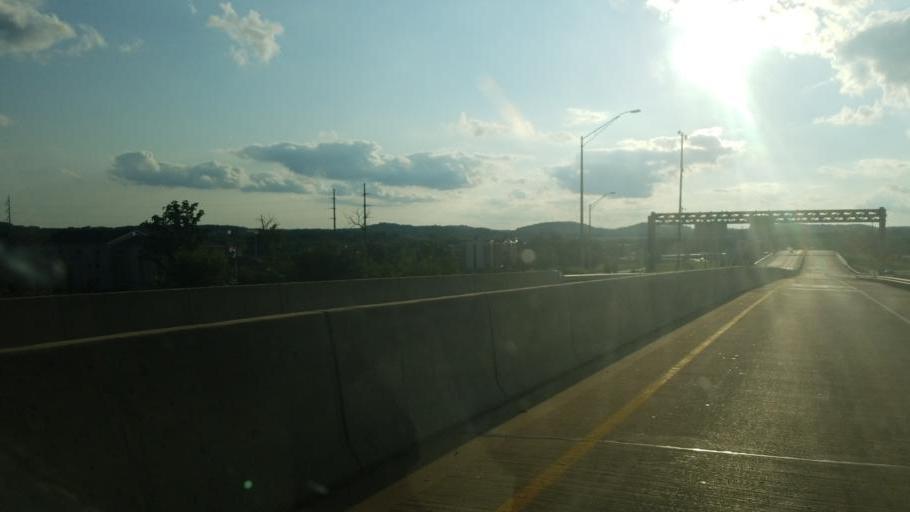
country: US
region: Pennsylvania
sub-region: Butler County
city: Cranberry Township
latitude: 40.6774
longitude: -80.0959
